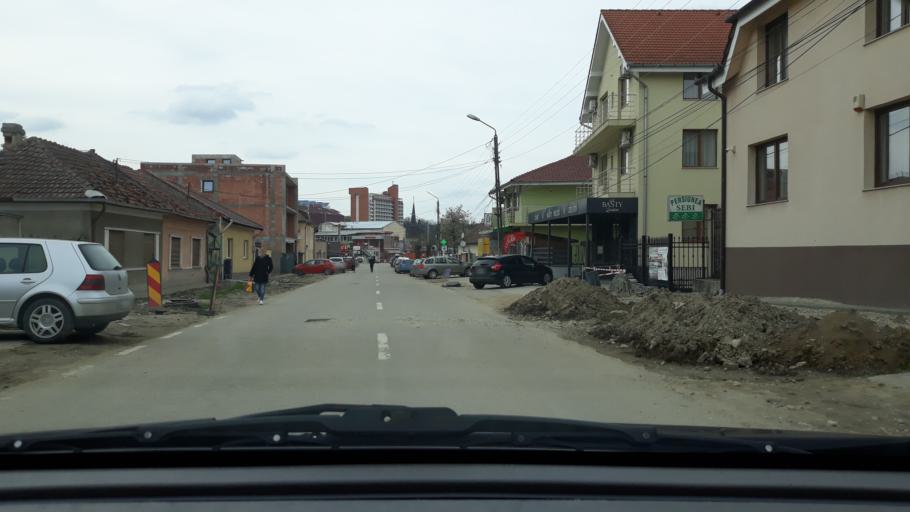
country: RO
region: Bihor
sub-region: Comuna Sanmartin
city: Sanmartin
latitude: 46.9879
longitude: 21.9819
